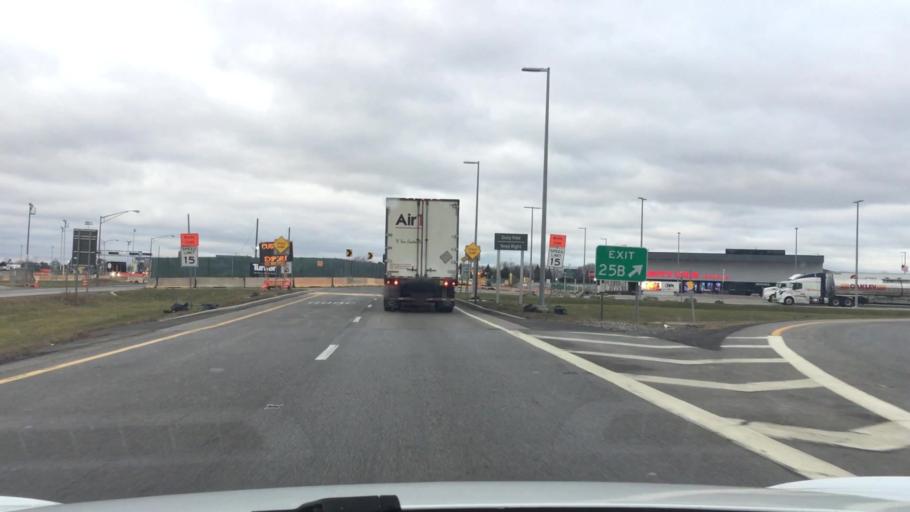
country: US
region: New York
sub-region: Niagara County
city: Lewiston
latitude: 43.1517
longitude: -79.0318
